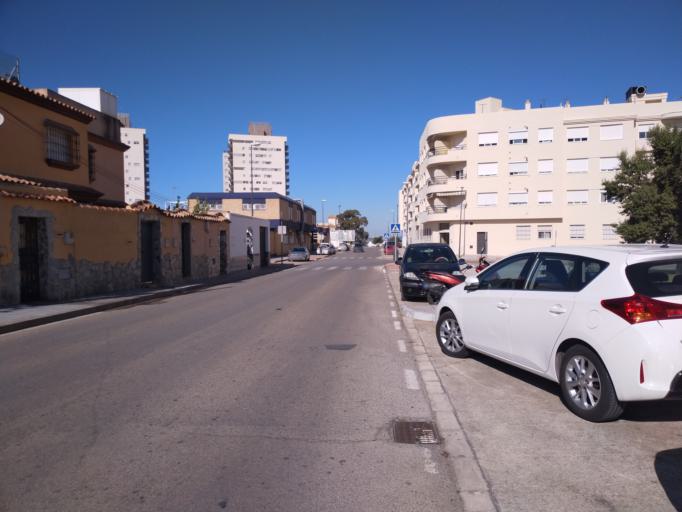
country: ES
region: Andalusia
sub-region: Provincia de Cadiz
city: San Fernando
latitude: 36.4815
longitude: -6.1980
